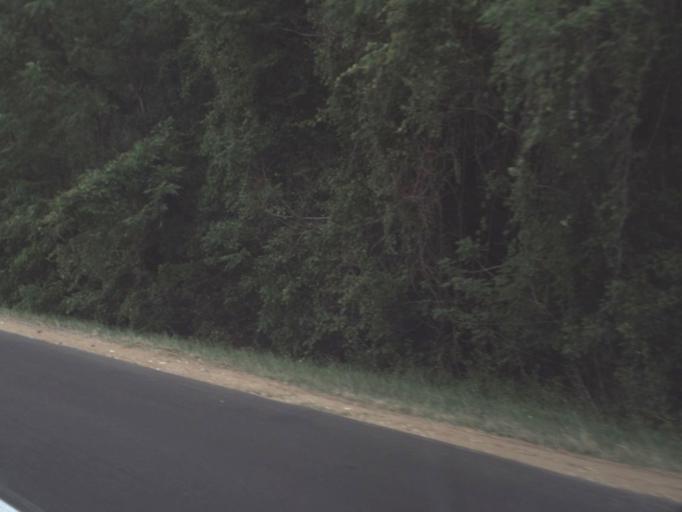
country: US
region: Florida
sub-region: Marion County
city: Citra
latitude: 29.3885
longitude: -82.2368
